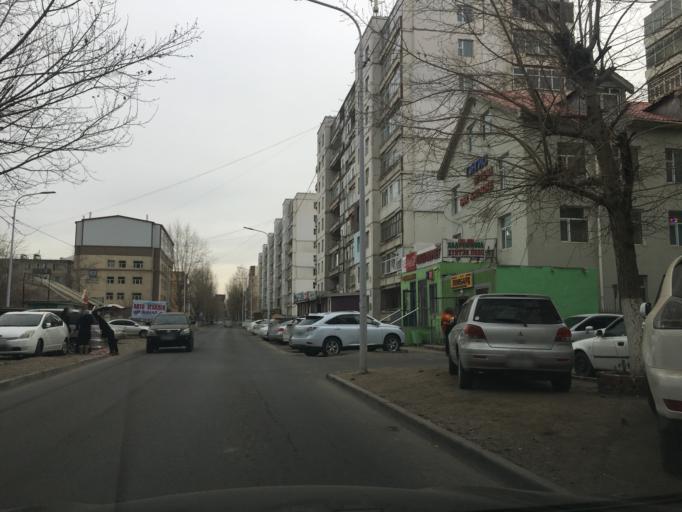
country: MN
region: Ulaanbaatar
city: Ulaanbaatar
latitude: 47.9107
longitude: 106.8891
